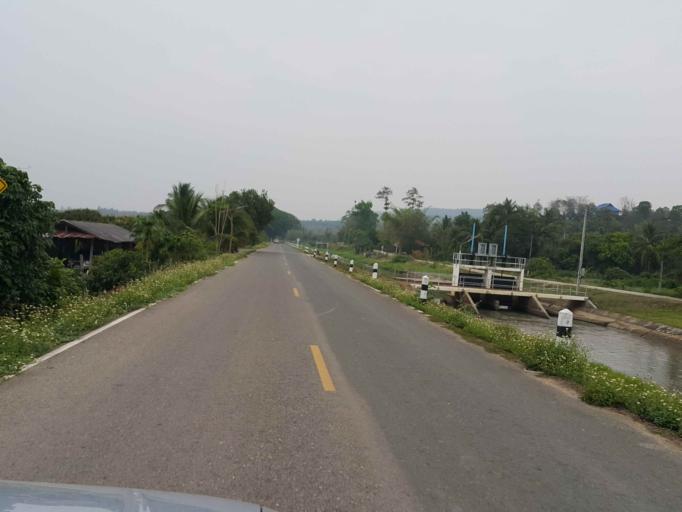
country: TH
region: Chiang Mai
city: Mae Taeng
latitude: 19.0501
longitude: 98.9752
